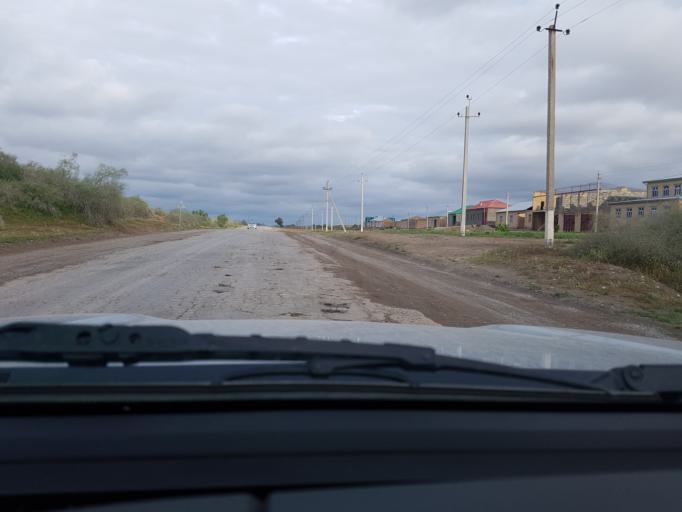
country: TM
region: Lebap
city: Atamyrat
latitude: 38.1123
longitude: 64.7371
